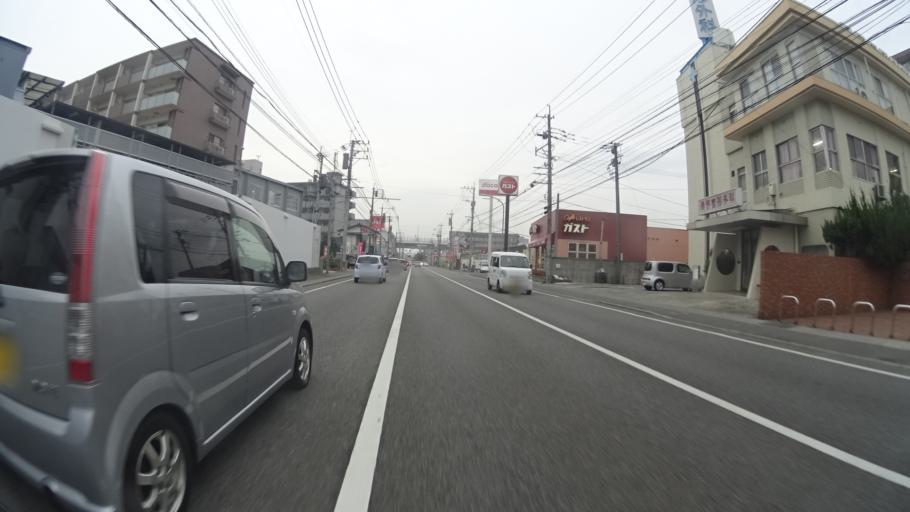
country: JP
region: Fukuoka
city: Onojo
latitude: 33.5452
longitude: 130.4464
